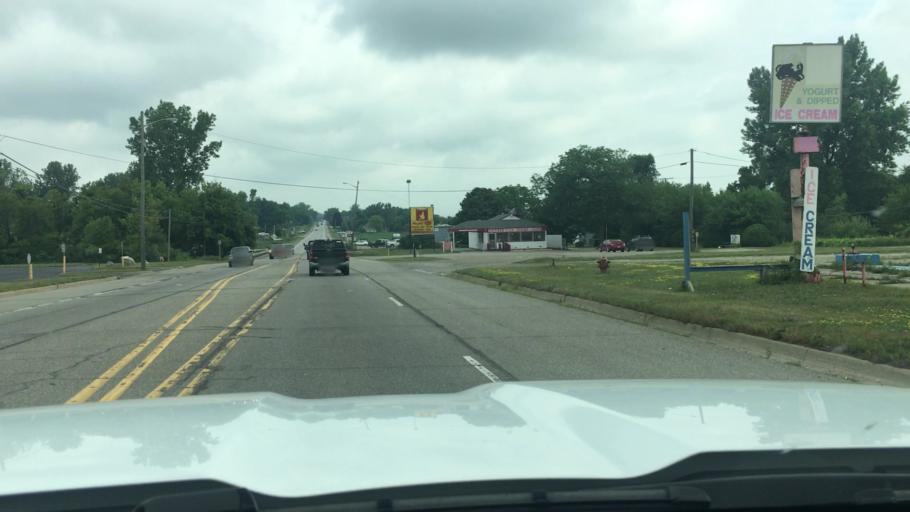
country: US
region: Michigan
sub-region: Lapeer County
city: Imlay City
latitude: 43.0315
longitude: -83.0715
